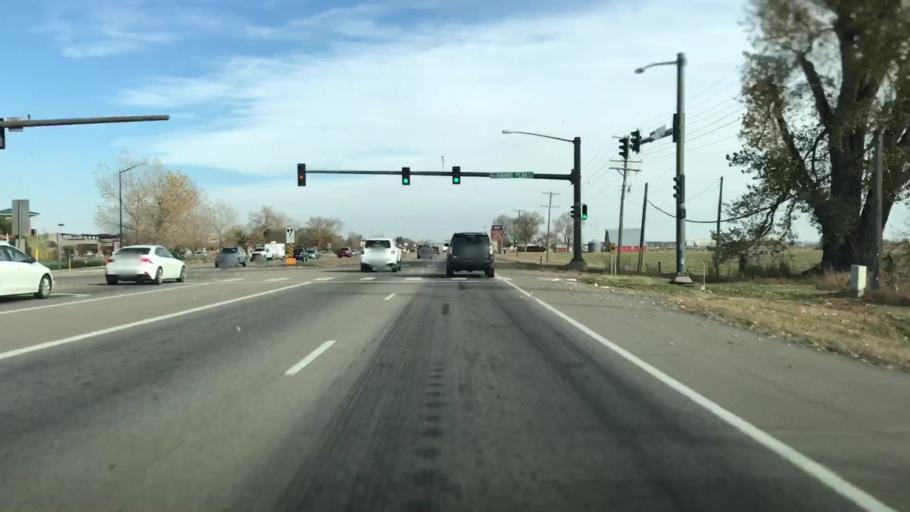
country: US
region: Colorado
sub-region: Larimer County
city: Loveland
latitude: 40.4071
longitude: -105.0119
